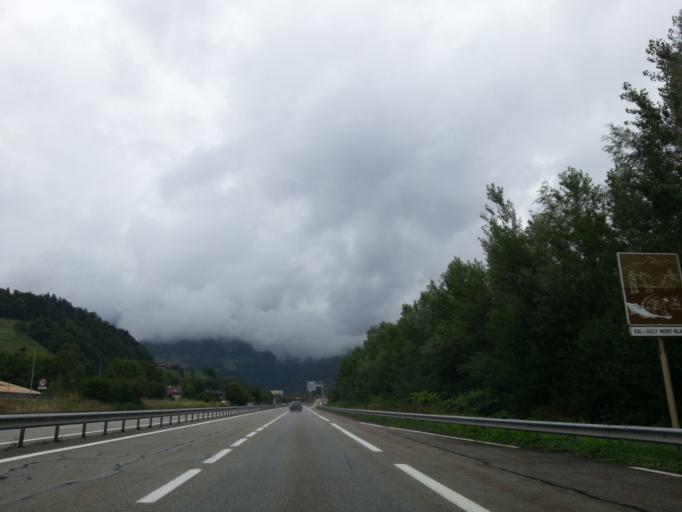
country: FR
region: Rhone-Alpes
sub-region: Departement de la Savoie
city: Marthod
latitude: 45.7262
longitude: 6.4155
